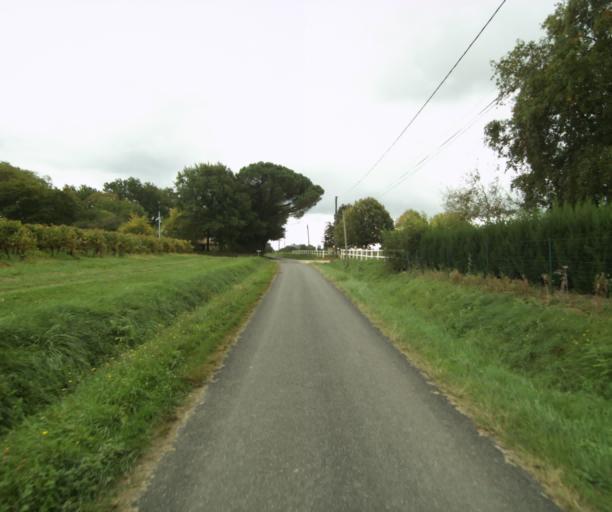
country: FR
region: Midi-Pyrenees
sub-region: Departement du Gers
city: Eauze
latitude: 43.8941
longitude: 0.0662
